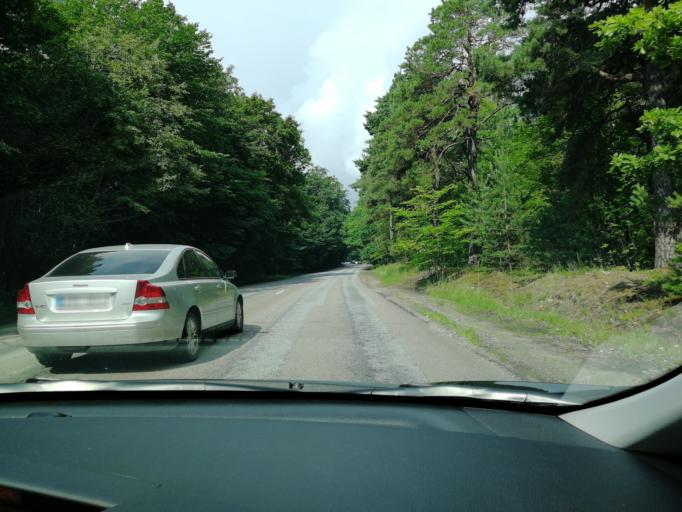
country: EE
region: Paernumaa
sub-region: Paernu linn
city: Parnu
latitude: 58.3825
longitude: 24.5448
